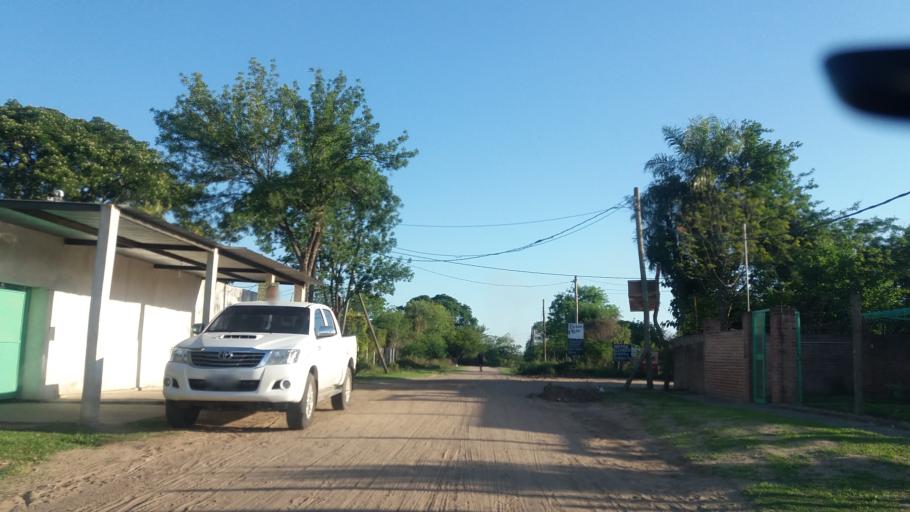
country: AR
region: Corrientes
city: Corrientes
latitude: -27.5142
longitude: -58.8320
